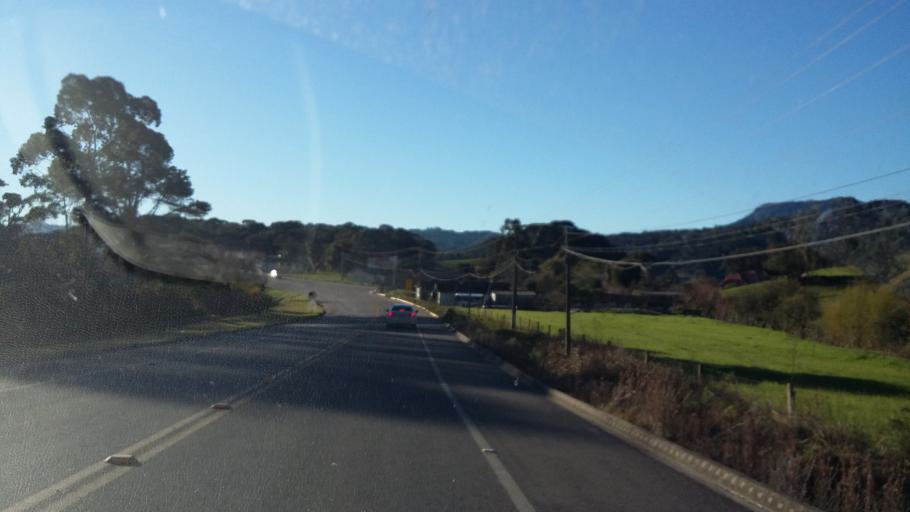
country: BR
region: Santa Catarina
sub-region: Lauro Muller
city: Lauro Muller
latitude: -28.0027
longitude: -49.5468
